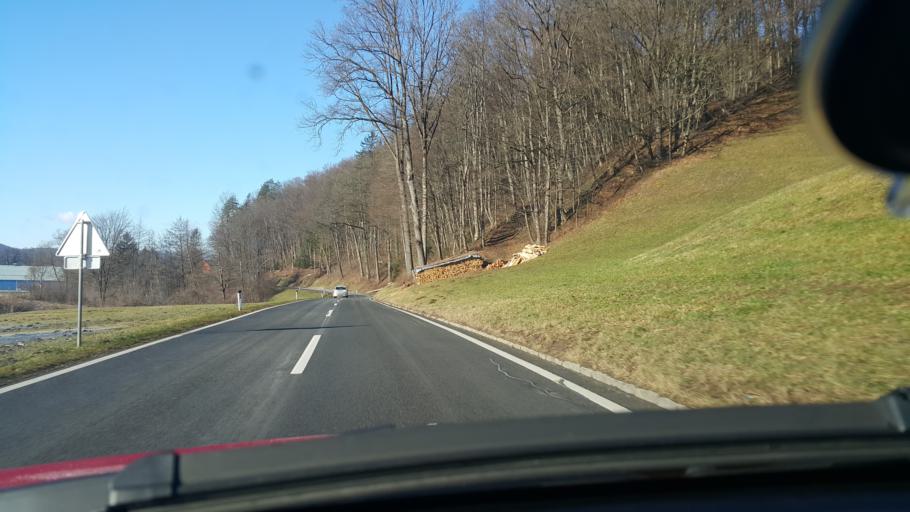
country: AT
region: Styria
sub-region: Politischer Bezirk Leibnitz
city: Arnfels
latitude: 46.6749
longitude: 15.4120
